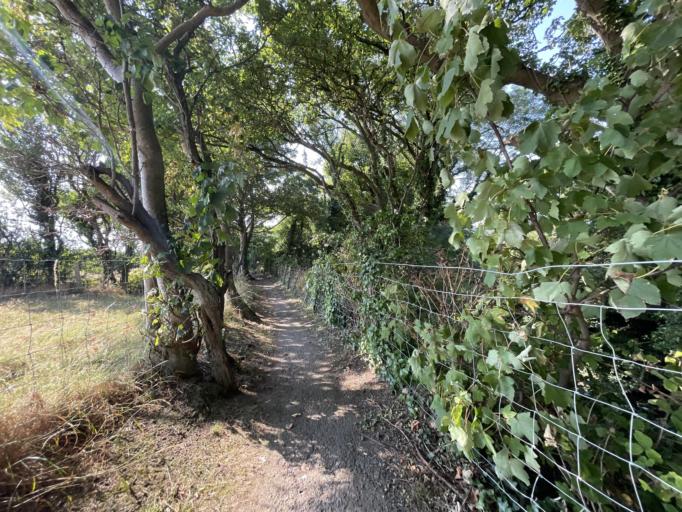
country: GB
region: Wales
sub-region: County of Ceredigion
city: Llanon
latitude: 52.2842
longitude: -4.1776
